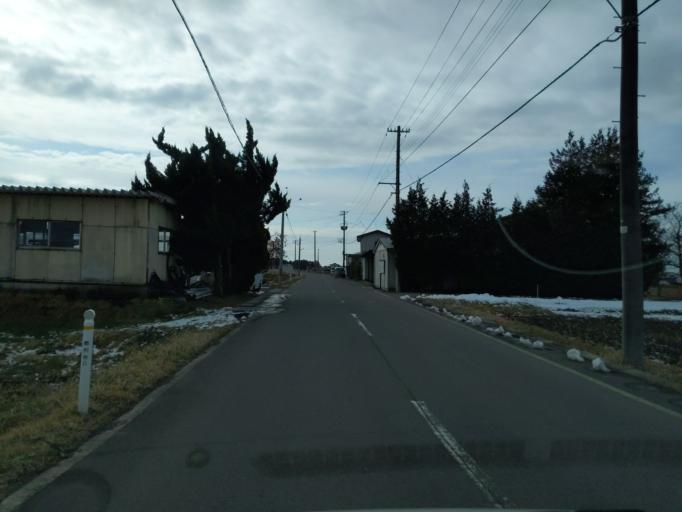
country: JP
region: Iwate
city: Mizusawa
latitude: 39.0928
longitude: 141.1772
